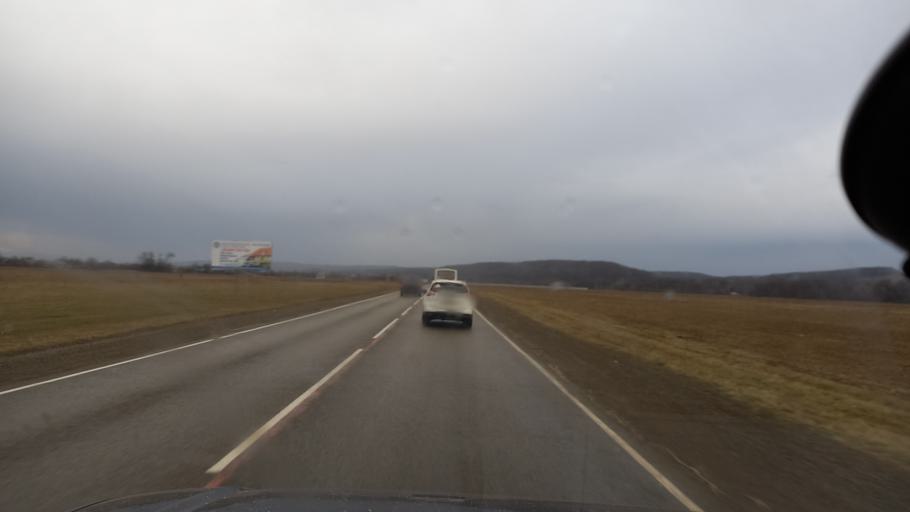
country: RU
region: Adygeya
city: Tul'skiy
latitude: 44.5369
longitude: 40.1402
